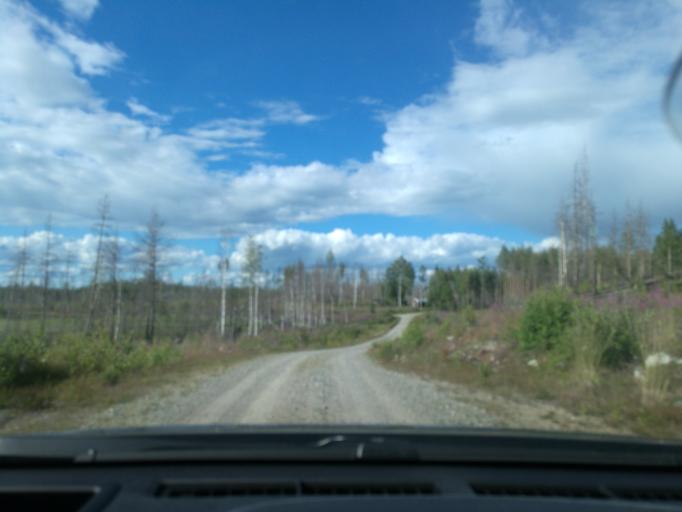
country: SE
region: Vaestmanland
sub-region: Surahammars Kommun
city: Ramnas
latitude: 59.8525
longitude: 16.2504
